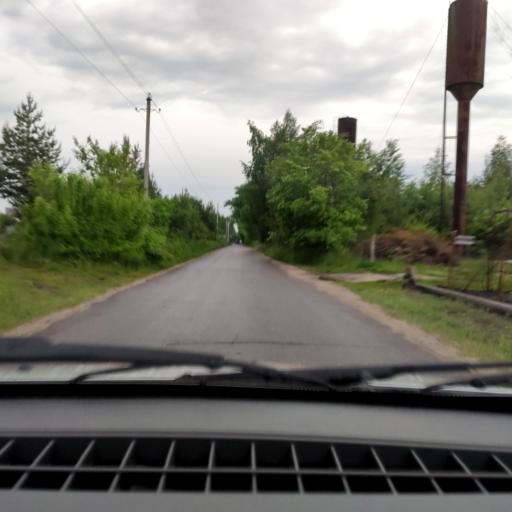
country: RU
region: Voronezj
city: Ramon'
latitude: 51.8520
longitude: 39.2402
